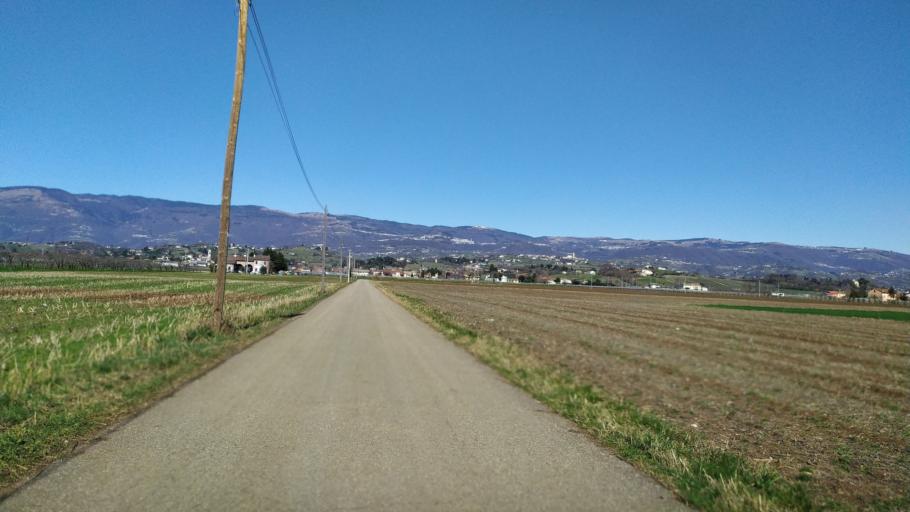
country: IT
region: Veneto
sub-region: Provincia di Vicenza
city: Breganze
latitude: 45.6894
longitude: 11.5752
